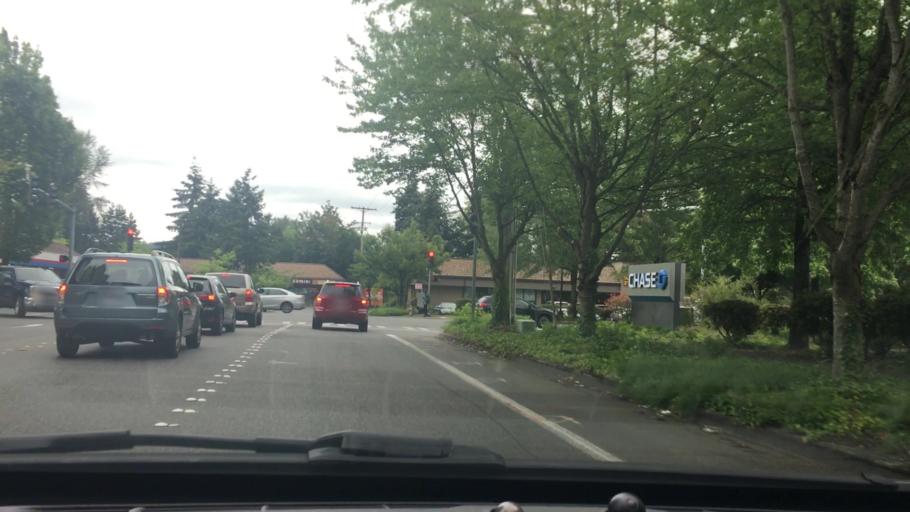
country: US
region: Washington
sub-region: King County
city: Issaquah
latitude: 47.5453
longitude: -122.0574
